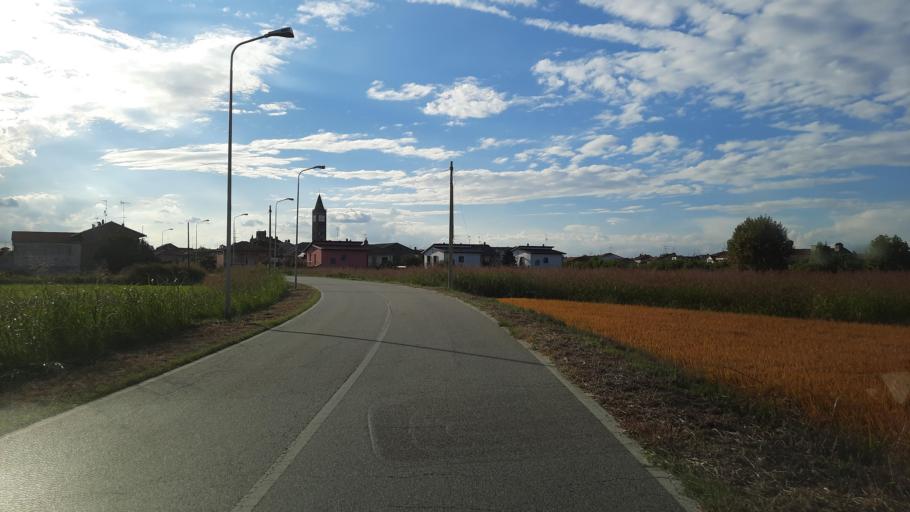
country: IT
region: Piedmont
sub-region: Provincia di Vercelli
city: Fontanetto Po
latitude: 45.1948
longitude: 8.1976
